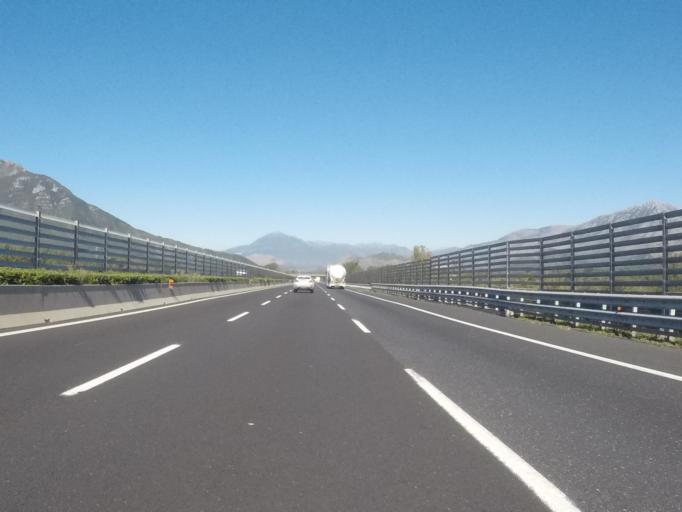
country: IT
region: Campania
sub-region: Provincia di Caserta
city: Mignano Monte Lungo
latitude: 41.3812
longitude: 14.0036
